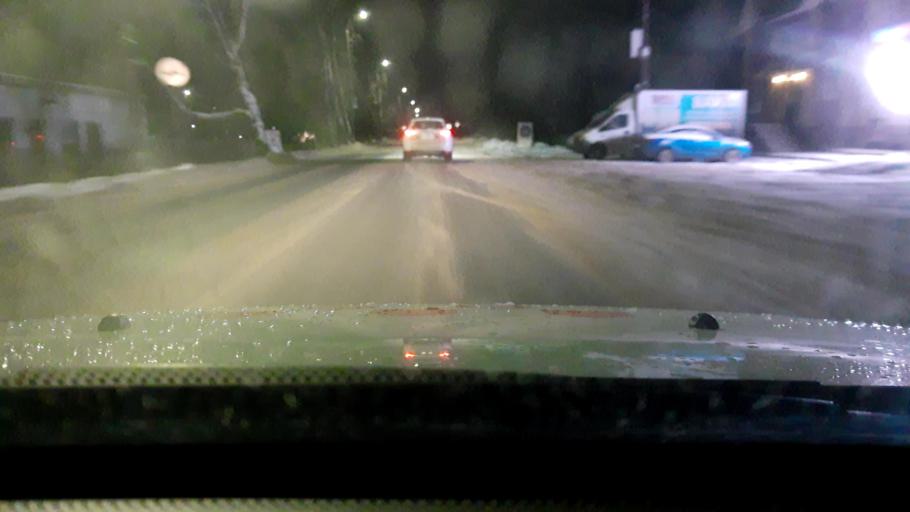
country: RU
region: Nizjnij Novgorod
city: Gorodets
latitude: 56.6538
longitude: 43.4902
